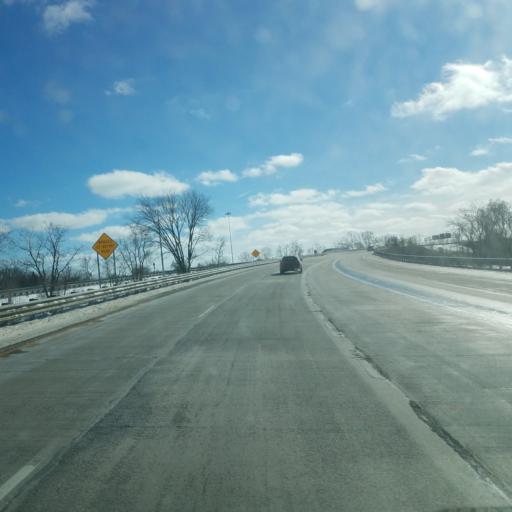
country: US
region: Michigan
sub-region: Ingham County
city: East Lansing
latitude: 42.7220
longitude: -84.5059
